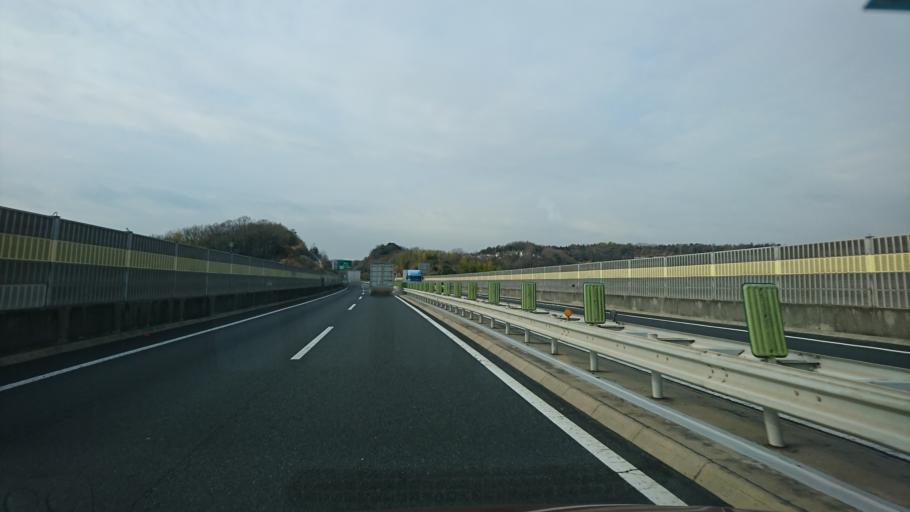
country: JP
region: Okayama
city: Okayama-shi
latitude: 34.7071
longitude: 133.8987
